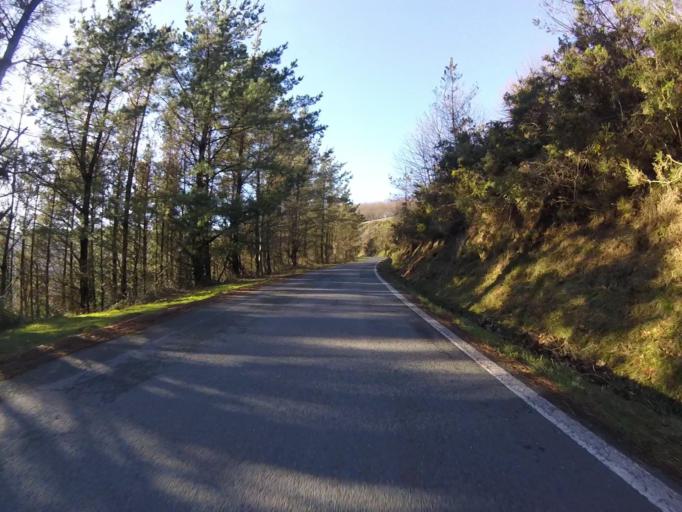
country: ES
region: Navarre
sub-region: Provincia de Navarra
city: Lesaka
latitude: 43.2679
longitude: -1.7456
